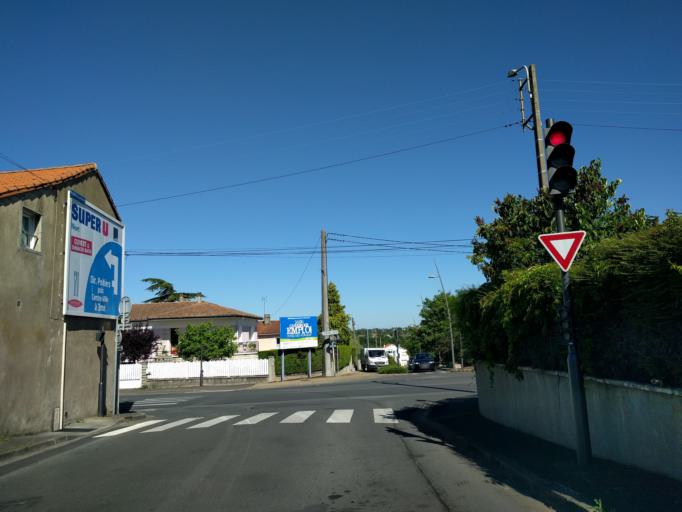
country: FR
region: Poitou-Charentes
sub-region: Departement des Deux-Sevres
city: Niort
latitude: 46.3388
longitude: -0.4463
